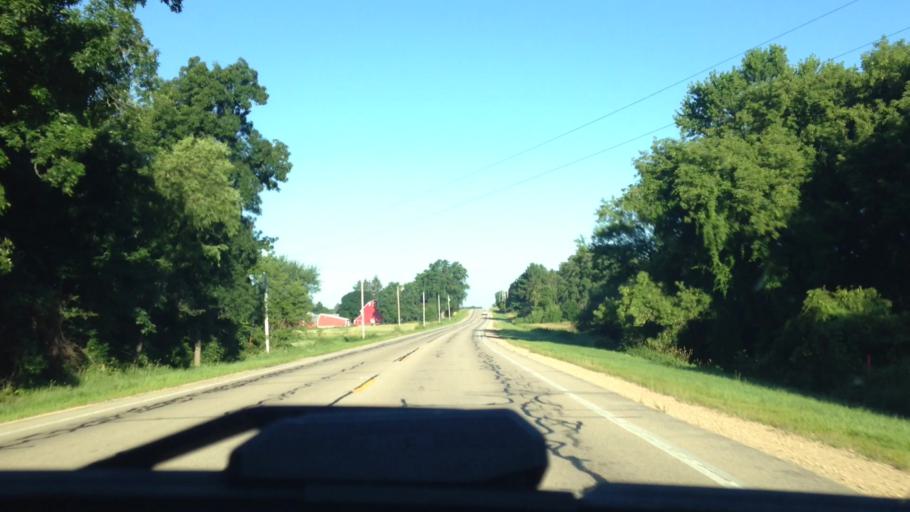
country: US
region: Wisconsin
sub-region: Columbia County
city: Fall River
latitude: 43.3404
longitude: -89.1505
